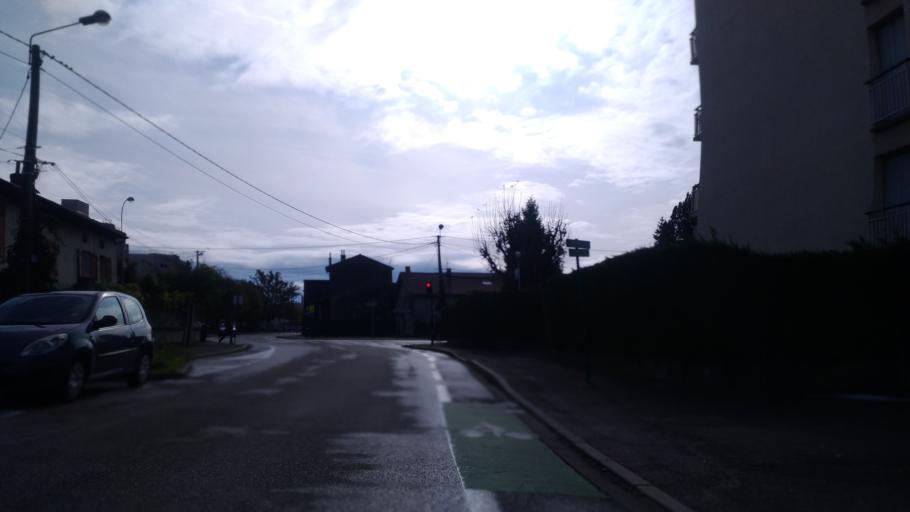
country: FR
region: Rhone-Alpes
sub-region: Departement de l'Isere
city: Fontaine
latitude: 45.1965
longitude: 5.6815
